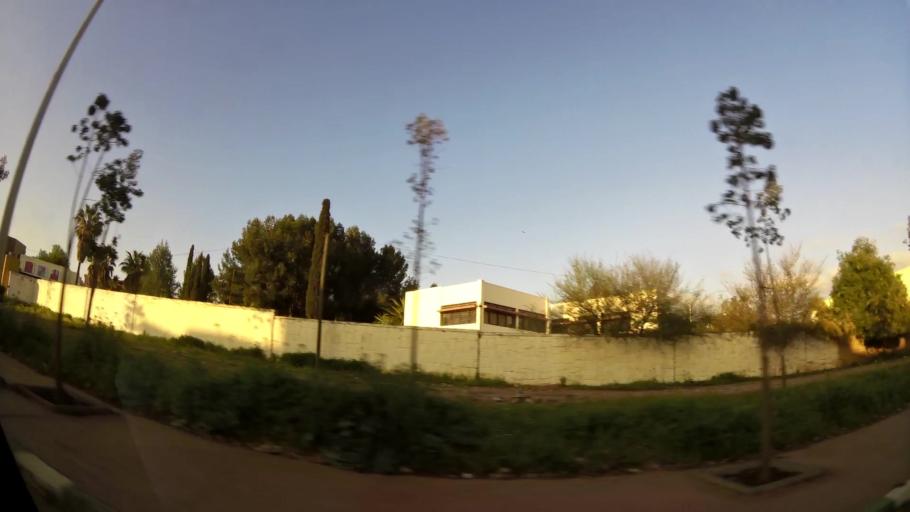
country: MA
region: Chaouia-Ouardigha
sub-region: Settat Province
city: Settat
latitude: 32.9904
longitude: -7.6115
